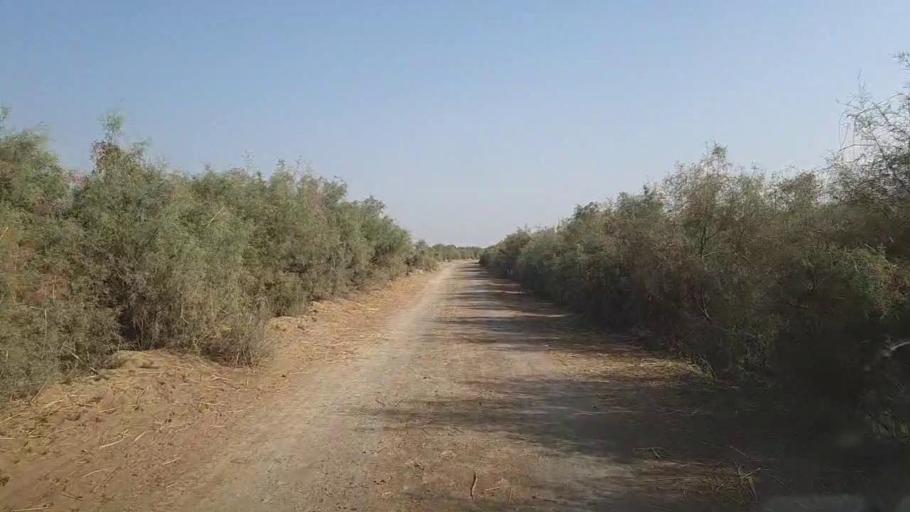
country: PK
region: Sindh
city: Kandhkot
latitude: 28.3581
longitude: 69.3320
